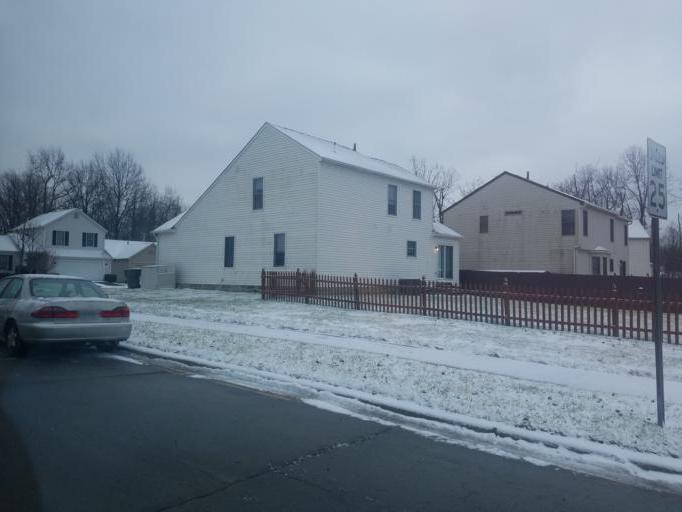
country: US
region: Ohio
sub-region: Franklin County
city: Reynoldsburg
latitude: 39.9954
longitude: -82.7782
